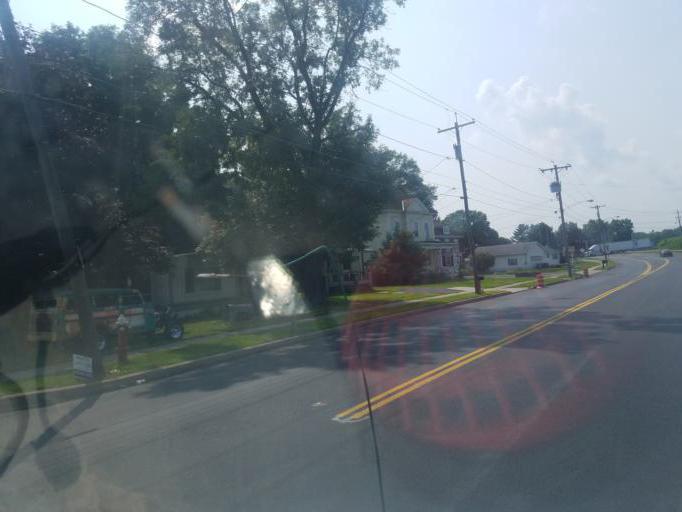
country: US
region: New York
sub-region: Montgomery County
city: Fonda
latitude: 42.9495
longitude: -74.3667
